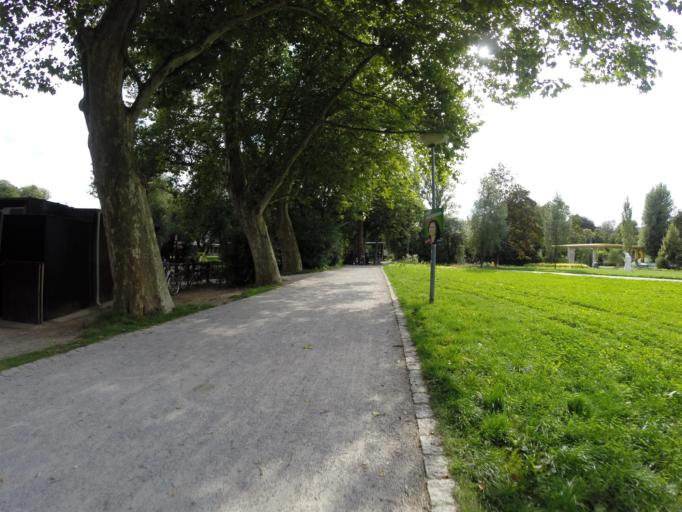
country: DE
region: Thuringia
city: Jena
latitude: 50.9233
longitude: 11.5851
